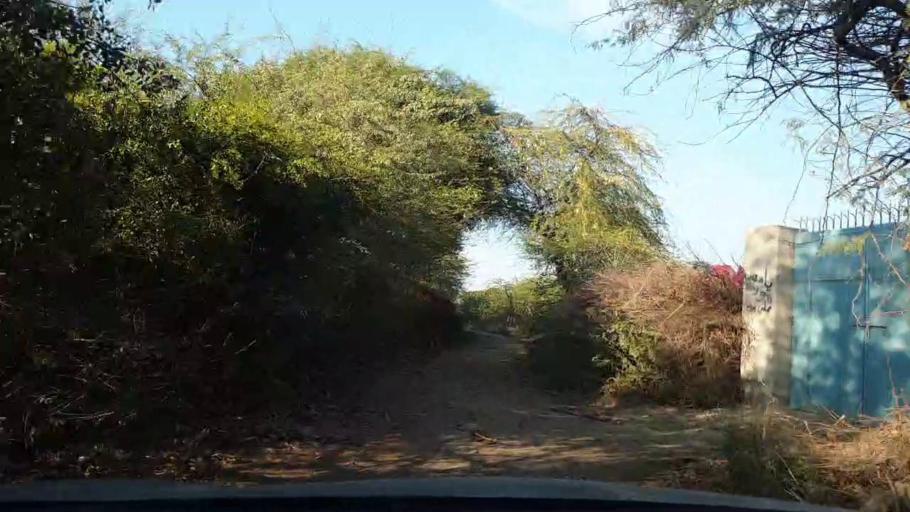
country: PK
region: Sindh
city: Tando Adam
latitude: 25.7013
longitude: 68.6923
